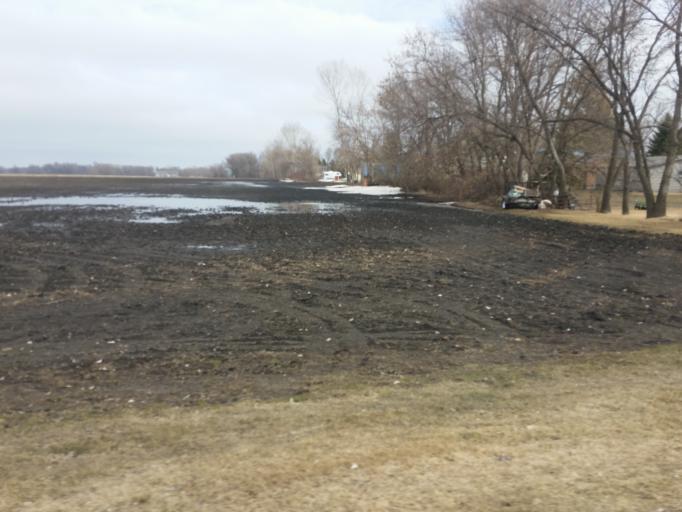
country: US
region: North Dakota
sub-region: Walsh County
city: Grafton
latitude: 48.4277
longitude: -97.3212
